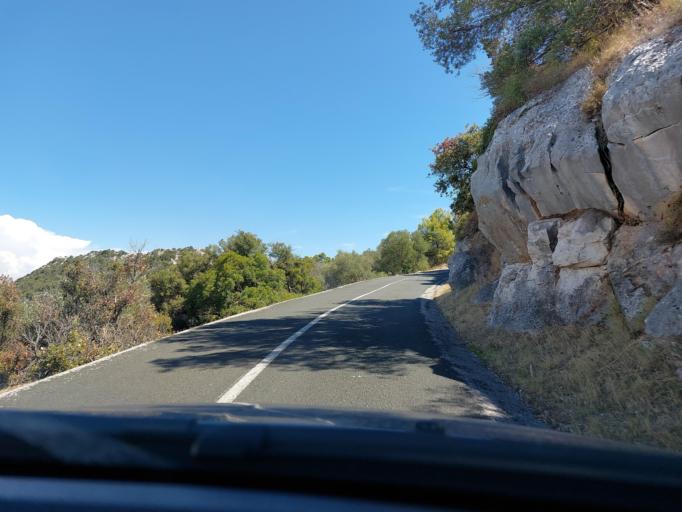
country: HR
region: Dubrovacko-Neretvanska
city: Smokvica
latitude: 42.7691
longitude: 16.8849
